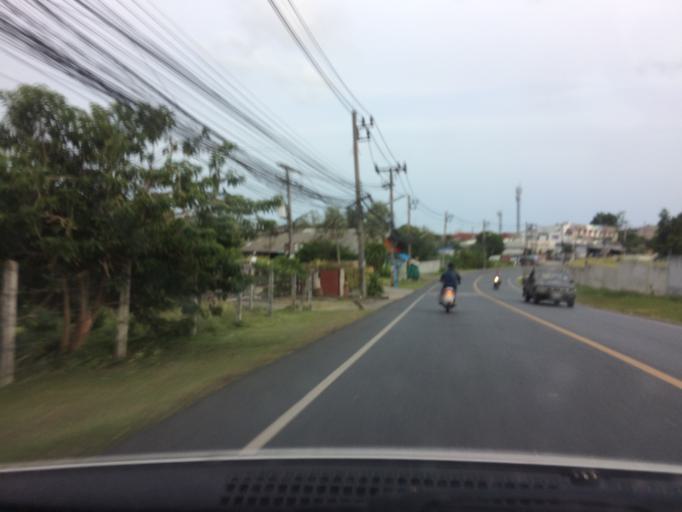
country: TH
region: Phuket
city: Ban Ratsada
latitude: 7.9015
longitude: 98.4107
